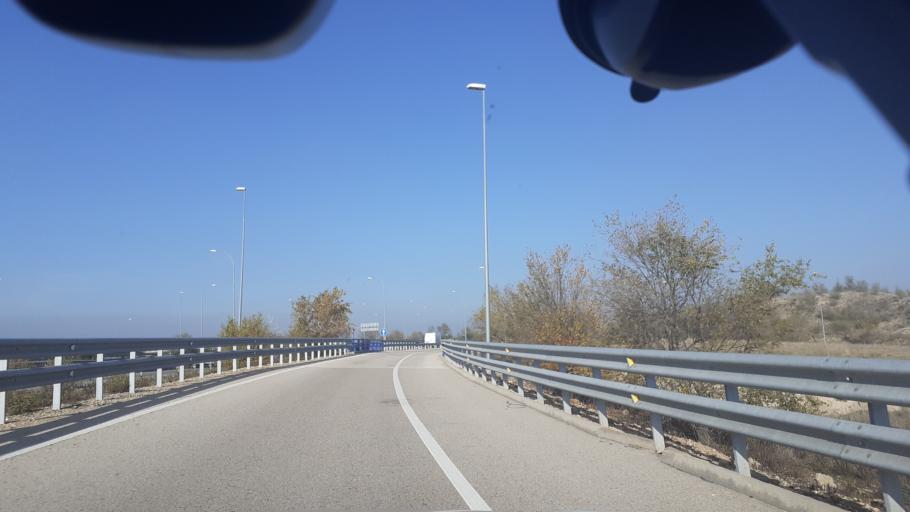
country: ES
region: Madrid
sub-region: Provincia de Madrid
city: Coslada
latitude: 40.4027
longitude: -3.5718
